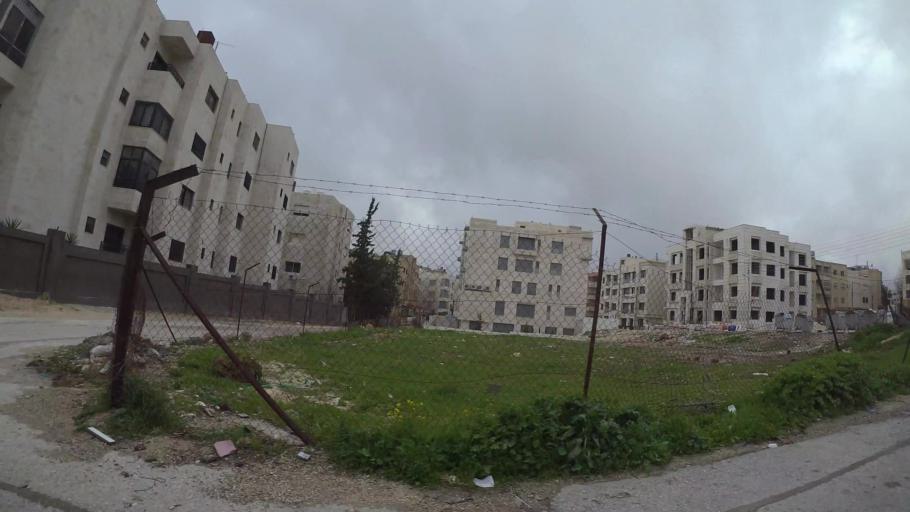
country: JO
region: Amman
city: Wadi as Sir
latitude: 31.9479
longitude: 35.8736
